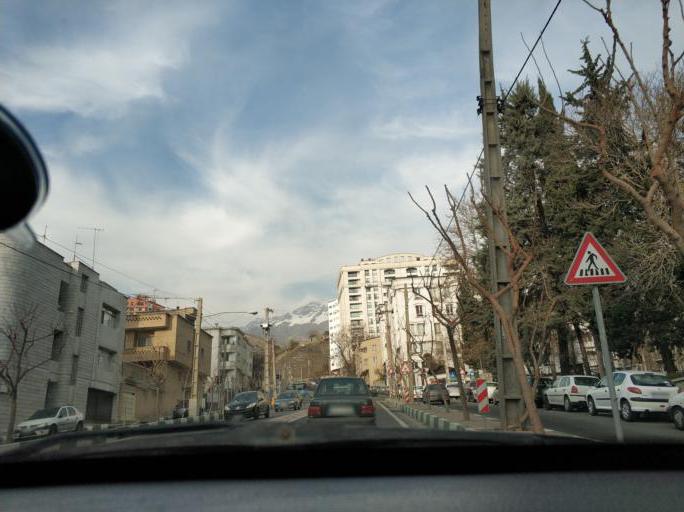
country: IR
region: Tehran
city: Tajrish
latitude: 35.8104
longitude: 51.4845
